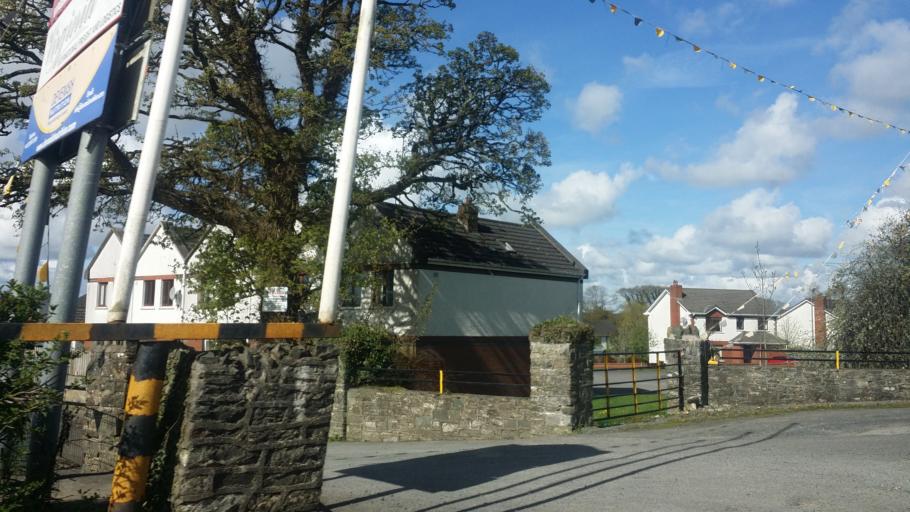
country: IE
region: Ulster
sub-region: An Cabhan
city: Virginia
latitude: 53.8317
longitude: -7.0700
